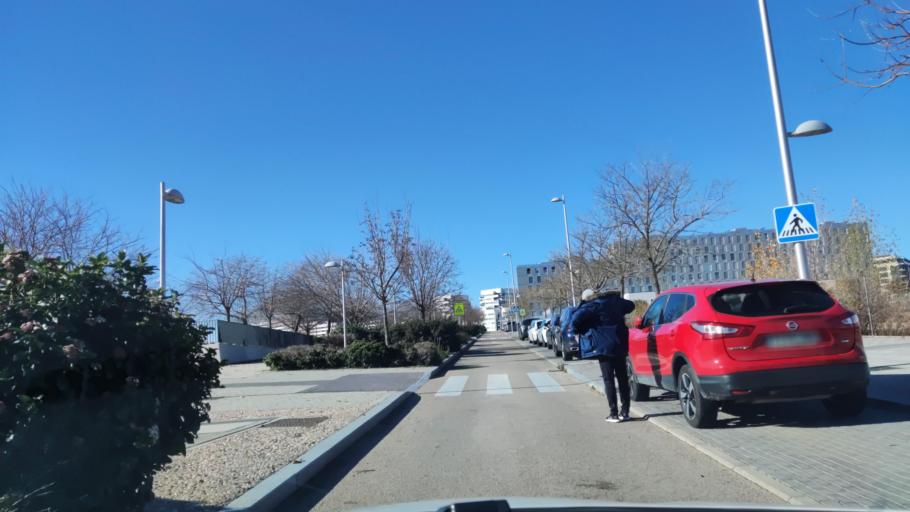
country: ES
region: Madrid
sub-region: Provincia de Madrid
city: Barajas de Madrid
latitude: 40.4863
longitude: -3.6093
